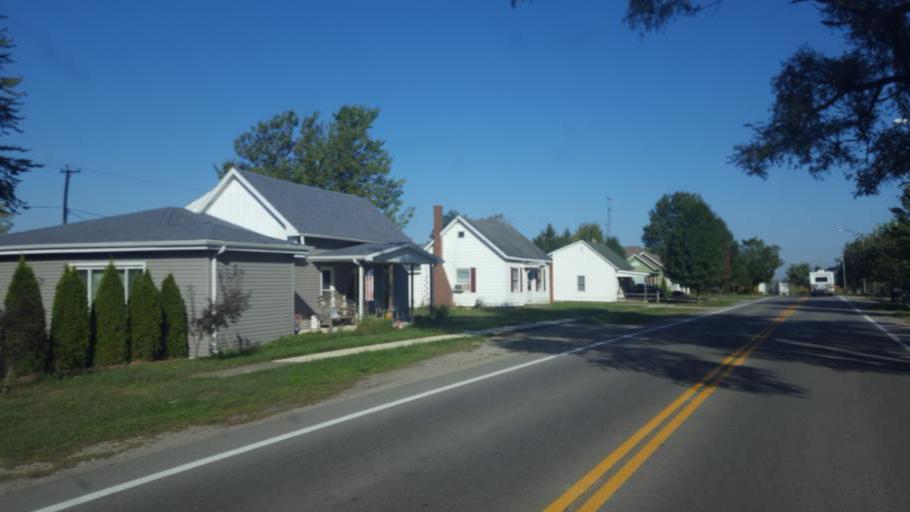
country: US
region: Ohio
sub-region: Hardin County
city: Kenton
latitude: 40.5375
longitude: -83.5227
